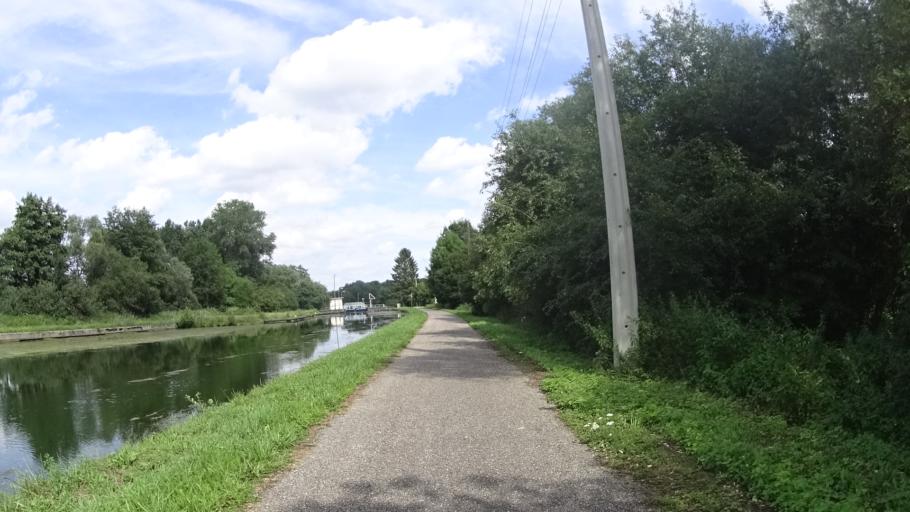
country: FR
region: Lorraine
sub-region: Departement de Meurthe-et-Moselle
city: Ecrouves
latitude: 48.6746
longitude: 5.8249
